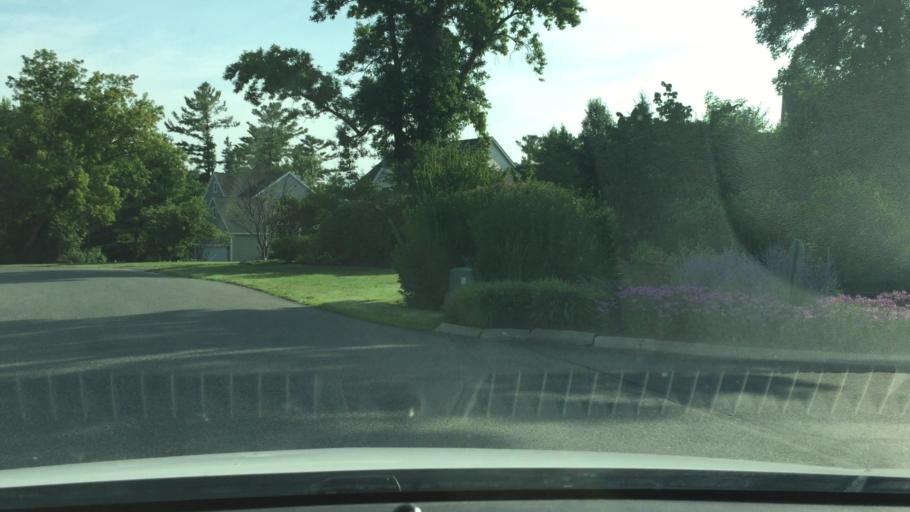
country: US
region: Massachusetts
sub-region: Berkshire County
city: Lenox
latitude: 42.3437
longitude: -73.2661
